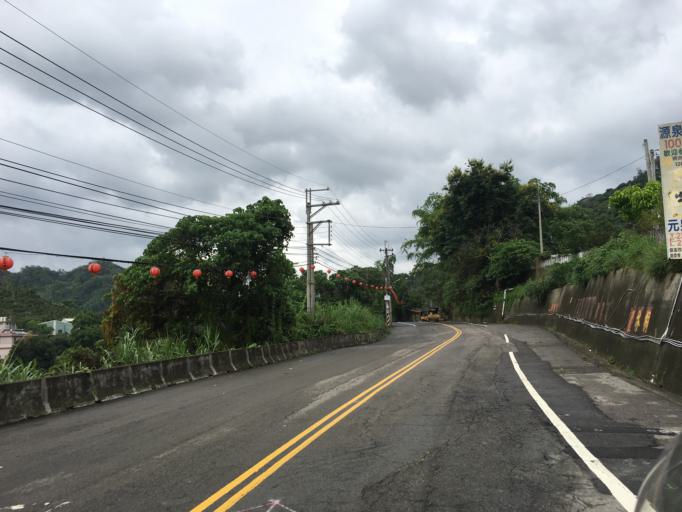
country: TW
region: Taiwan
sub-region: Taichung City
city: Taichung
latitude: 24.0750
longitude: 120.7261
